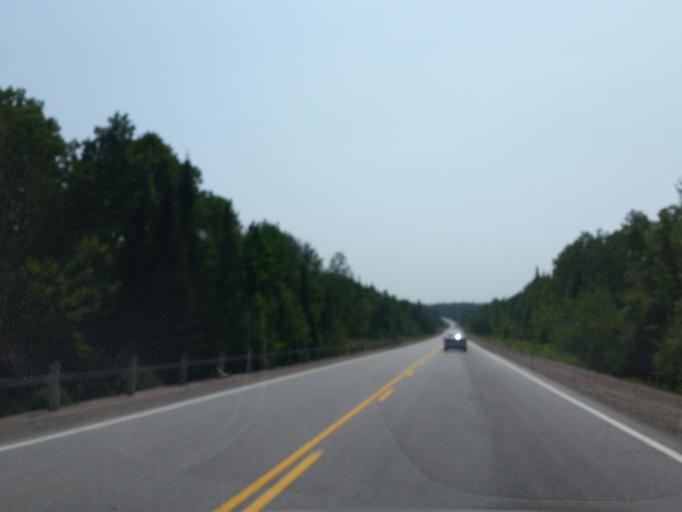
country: CA
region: Ontario
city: Mattawa
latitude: 46.2832
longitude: -78.5042
